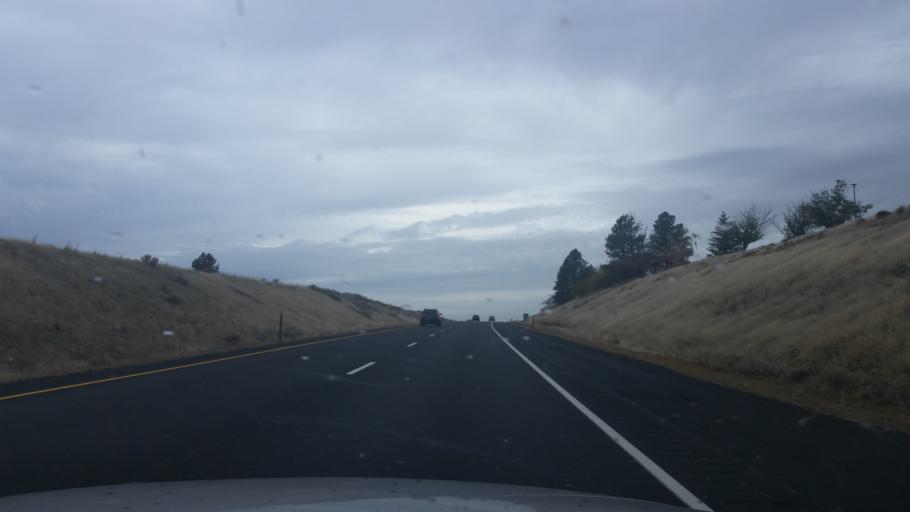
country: US
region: Washington
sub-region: Grant County
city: Warden
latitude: 47.0862
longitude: -118.8429
